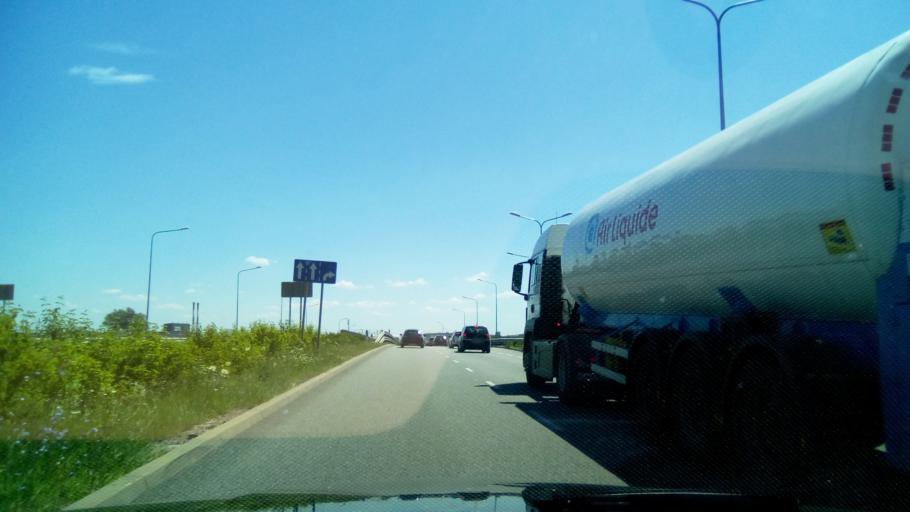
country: PL
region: Masovian Voivodeship
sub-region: Radom
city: Radom
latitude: 51.4199
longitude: 21.1851
